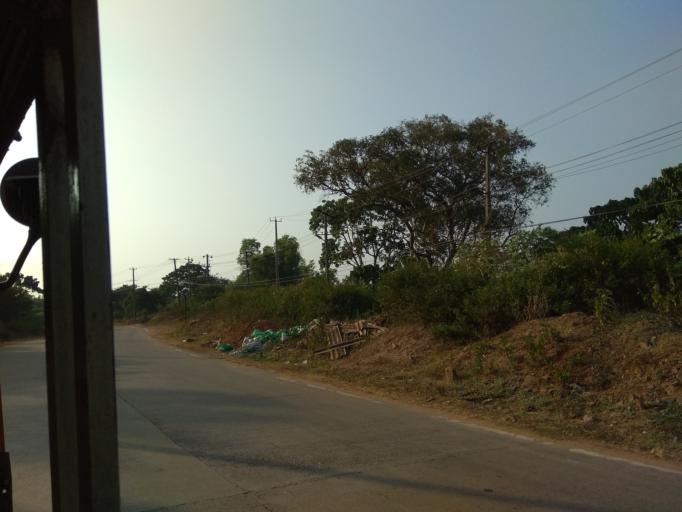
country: IN
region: Karnataka
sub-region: Dakshina Kannada
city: Mangalore
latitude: 12.9167
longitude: 74.8578
